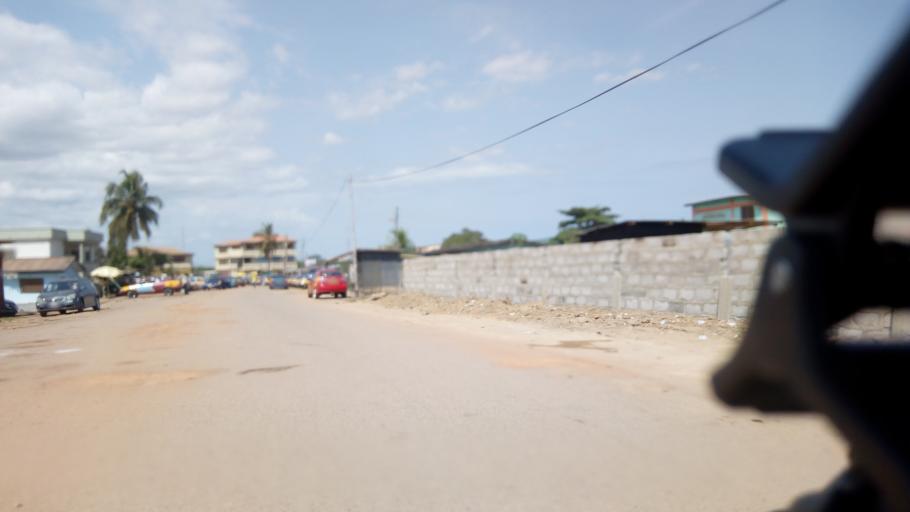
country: GH
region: Central
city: Cape Coast
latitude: 5.1334
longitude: -1.2783
